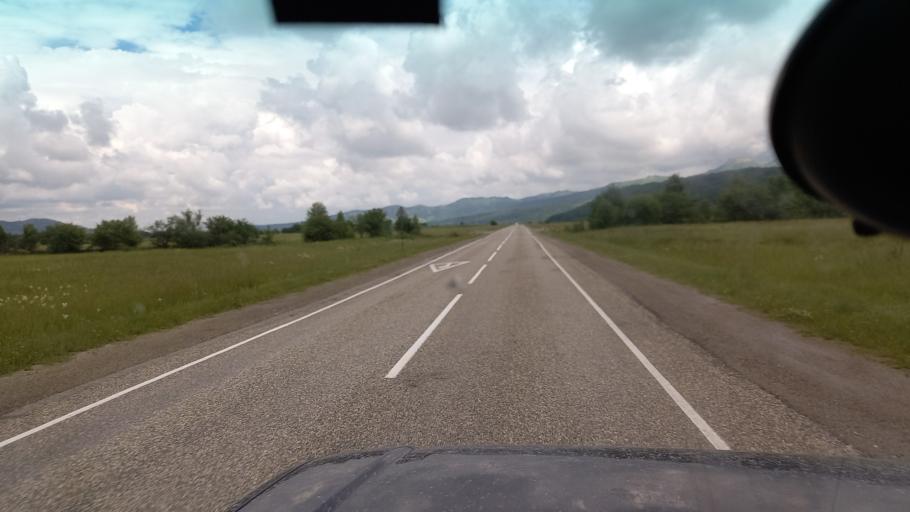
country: RU
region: Krasnodarskiy
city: Psebay
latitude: 44.0905
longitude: 40.8011
